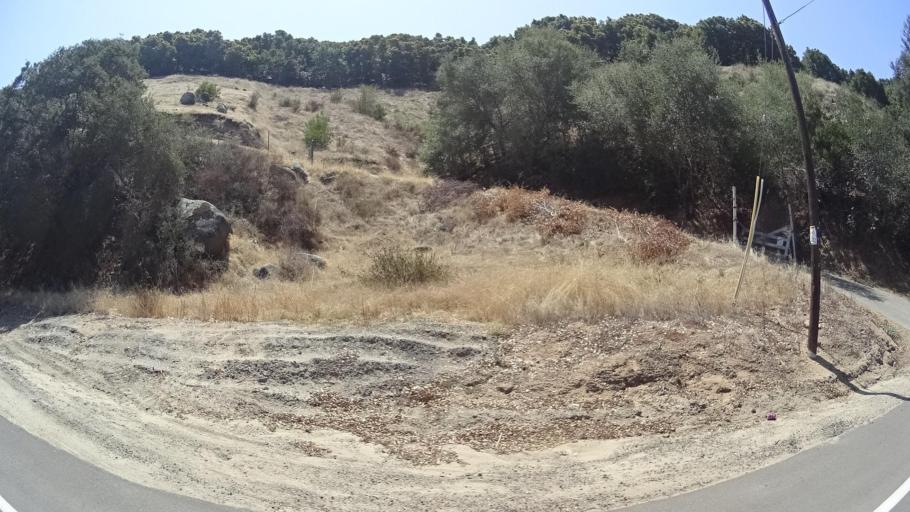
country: US
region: California
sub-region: San Diego County
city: Hidden Meadows
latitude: 33.2665
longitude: -117.1613
